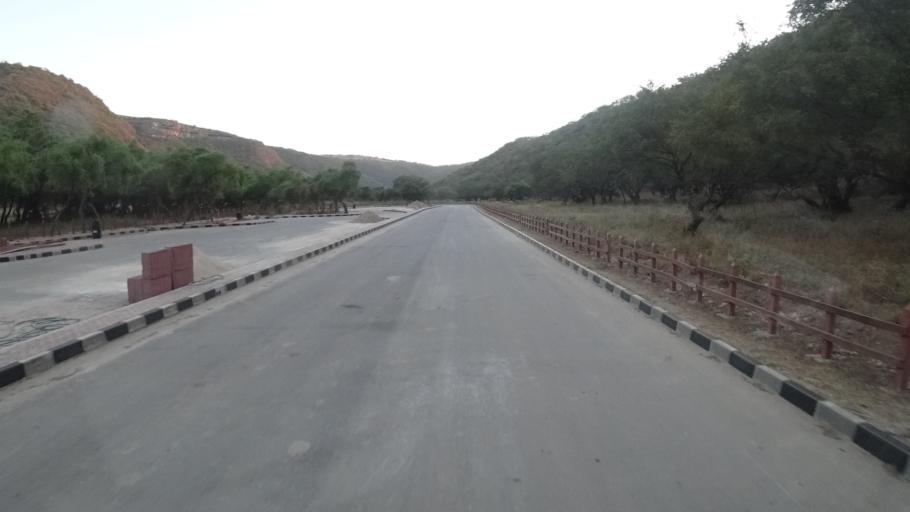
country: OM
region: Zufar
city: Salalah
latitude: 17.1025
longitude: 54.4517
